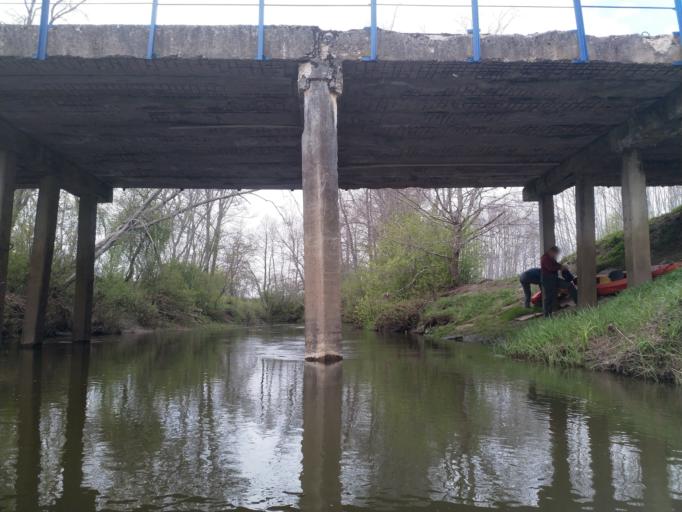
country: LV
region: Alsunga
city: Alsunga
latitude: 57.1257
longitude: 21.5499
